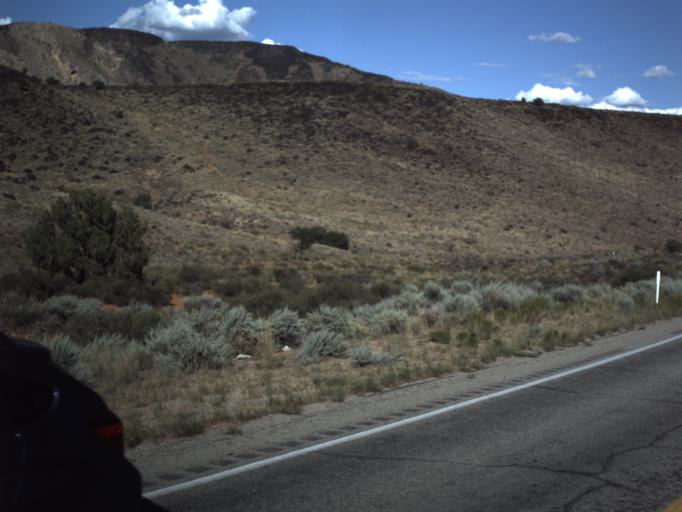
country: US
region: Utah
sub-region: Washington County
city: Toquerville
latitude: 37.2754
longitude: -113.3018
